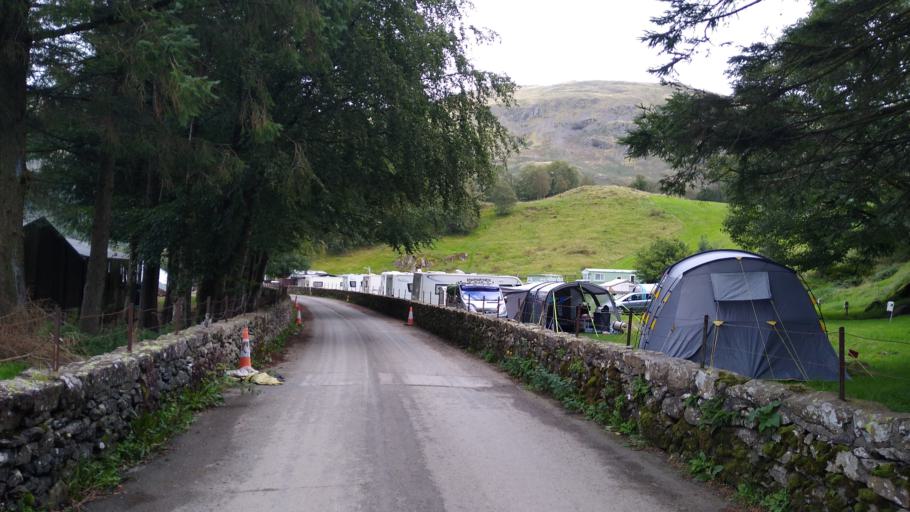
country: GB
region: England
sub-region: Cumbria
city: Keswick
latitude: 54.5642
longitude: -3.0634
